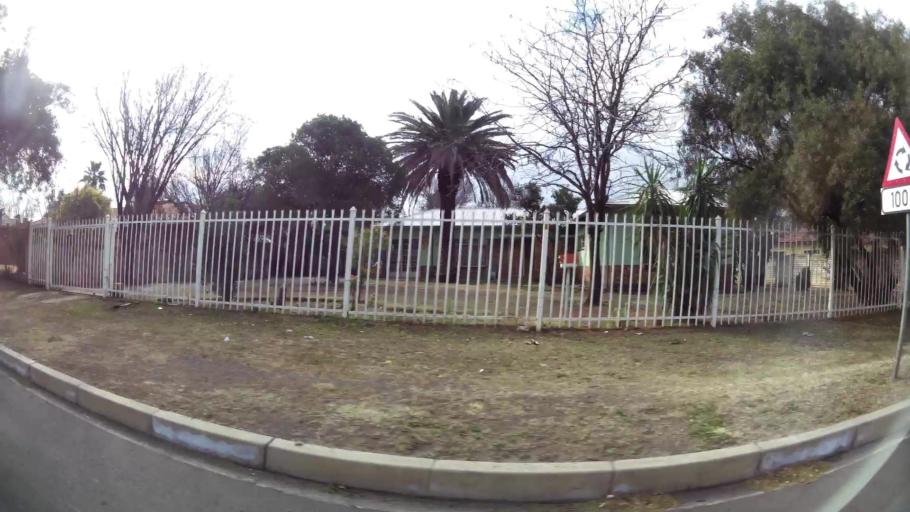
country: ZA
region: Orange Free State
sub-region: Mangaung Metropolitan Municipality
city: Bloemfontein
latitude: -29.0916
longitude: 26.2506
